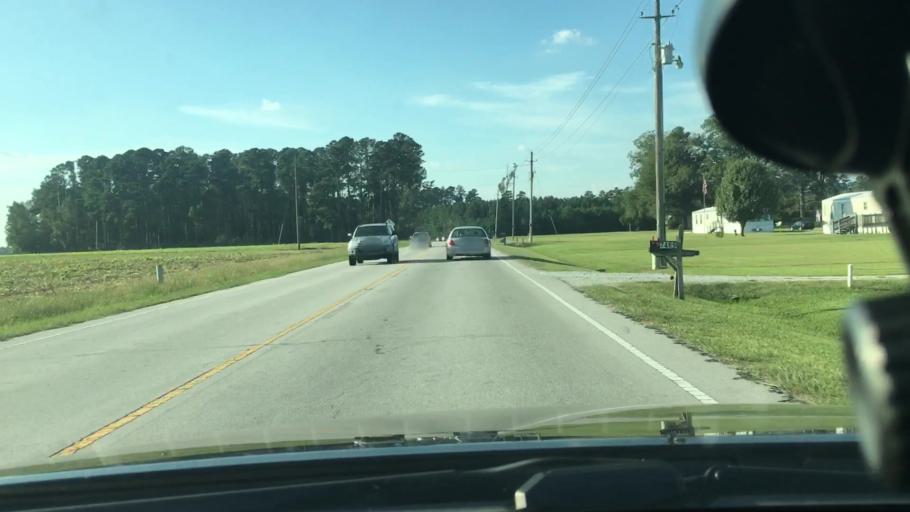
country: US
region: North Carolina
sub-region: Pitt County
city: Windsor
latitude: 35.4662
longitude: -77.2767
